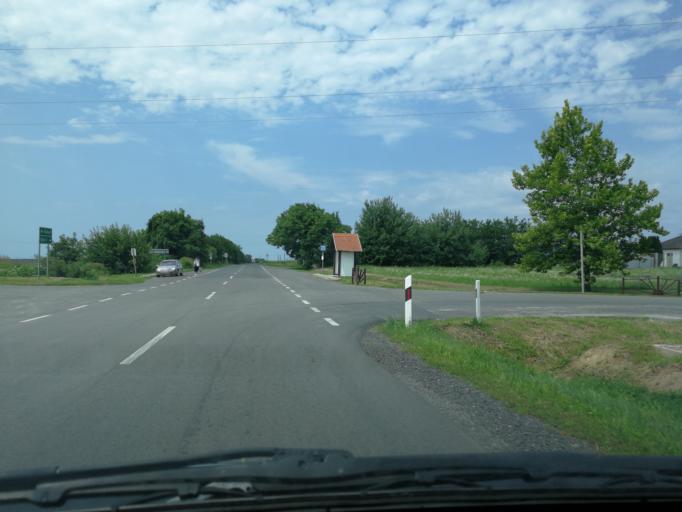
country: HU
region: Baranya
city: Siklos
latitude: 45.8494
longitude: 18.3572
